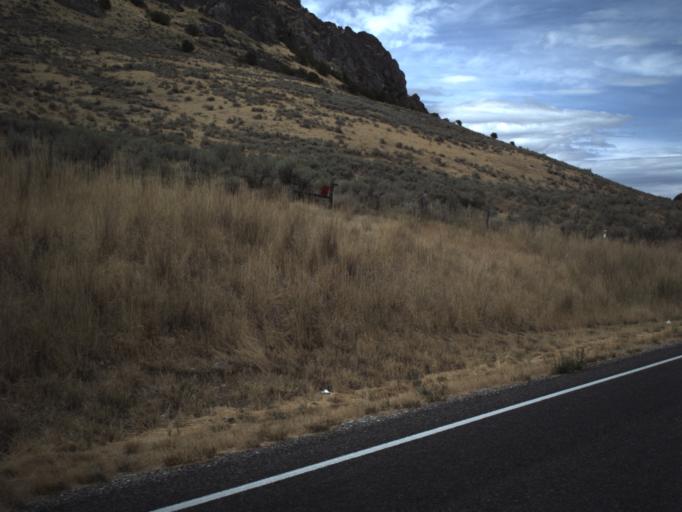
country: US
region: Utah
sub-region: Cache County
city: Benson
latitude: 41.8995
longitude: -111.9508
